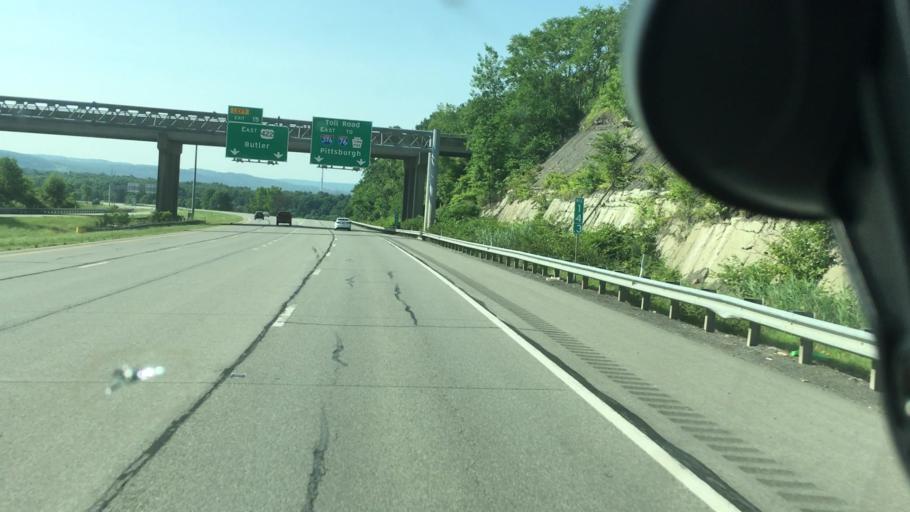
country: US
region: Pennsylvania
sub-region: Lawrence County
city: Oakwood
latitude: 40.9971
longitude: -80.3927
